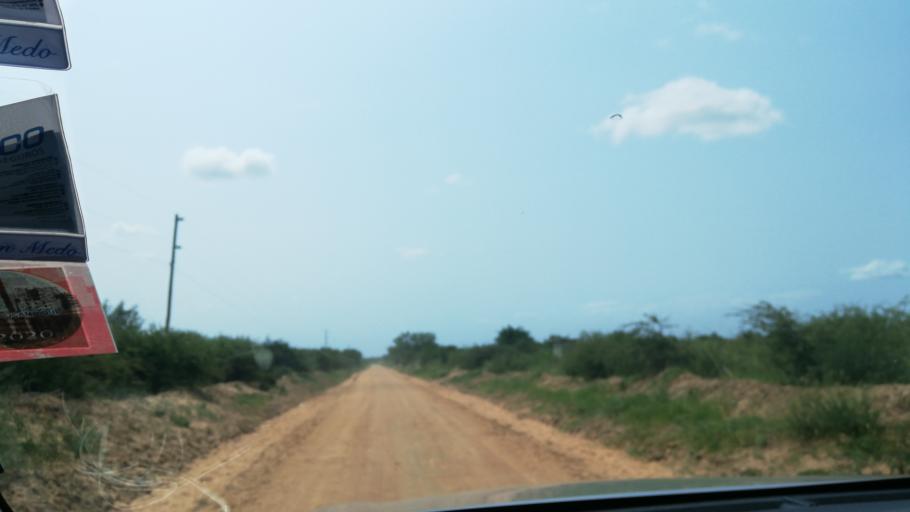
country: MZ
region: Maputo
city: Matola
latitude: -26.0920
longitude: 32.3905
